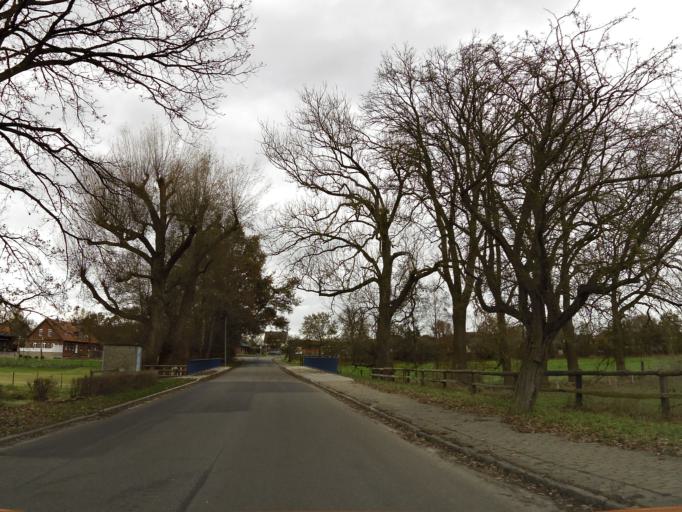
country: DE
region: Lower Saxony
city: Suderburg
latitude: 52.9526
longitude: 10.4834
